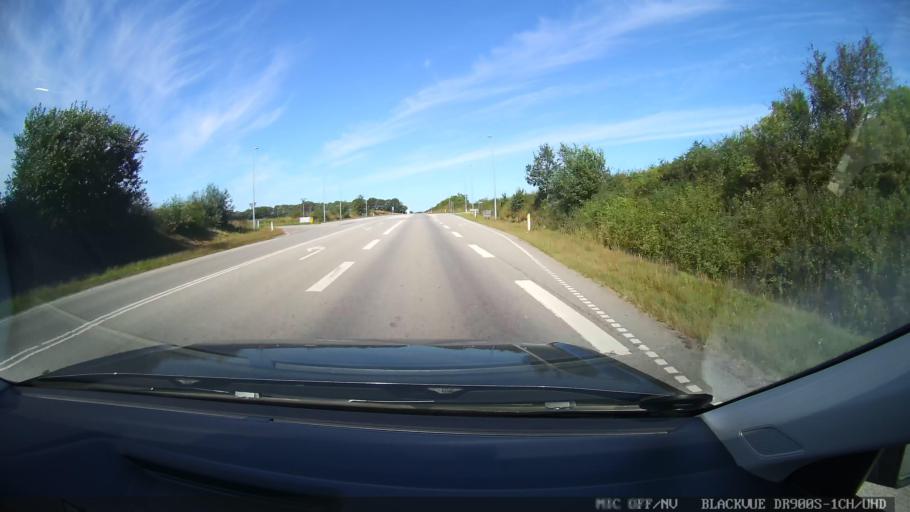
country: DK
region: North Denmark
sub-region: Mariagerfjord Kommune
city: Hobro
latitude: 56.6609
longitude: 9.7822
